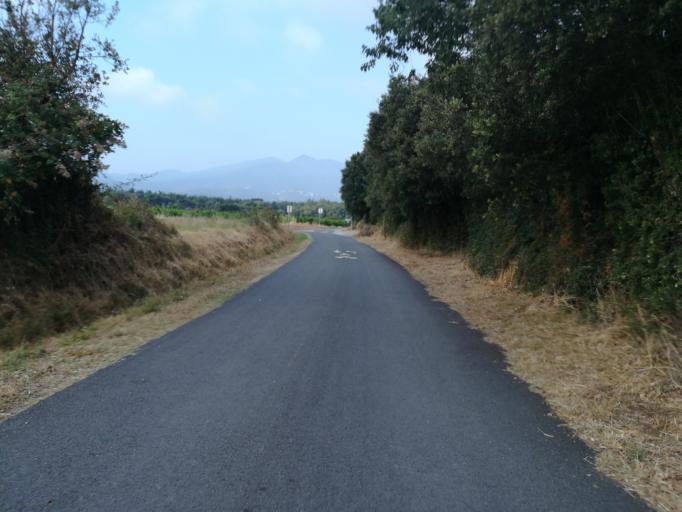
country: FR
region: Languedoc-Roussillon
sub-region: Departement des Pyrenees-Orientales
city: Maureillas-las-Illas
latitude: 42.5095
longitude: 2.8153
